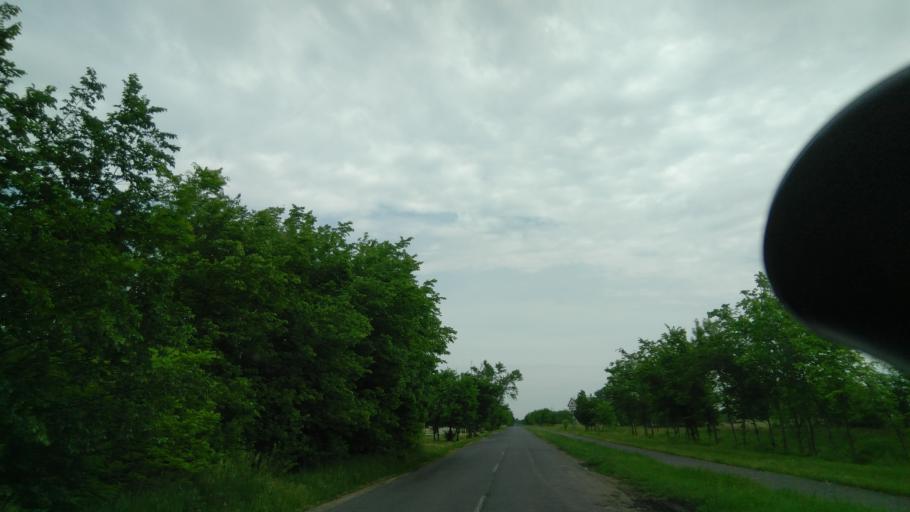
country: HU
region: Bekes
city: Szeghalom
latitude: 47.0388
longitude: 21.1838
